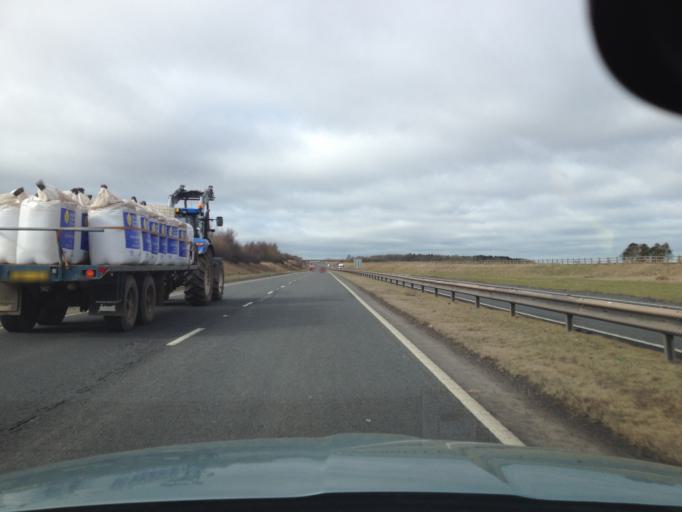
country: GB
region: Scotland
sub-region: East Lothian
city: Haddington
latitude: 55.9544
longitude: -2.8246
